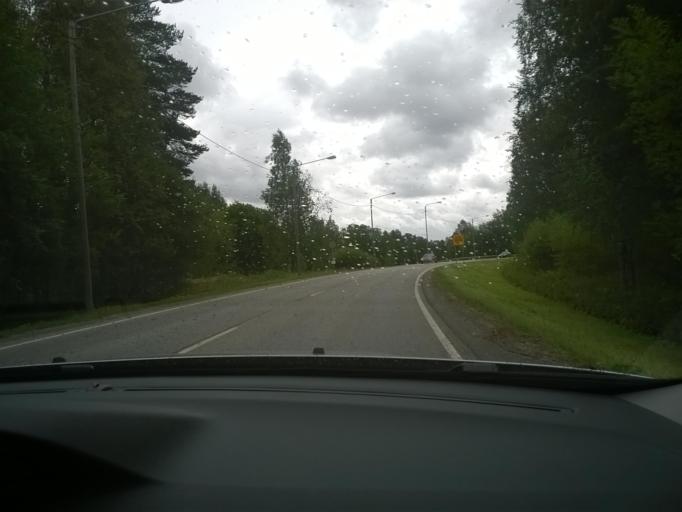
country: FI
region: Kainuu
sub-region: Kehys-Kainuu
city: Kuhmo
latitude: 64.1295
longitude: 29.5005
